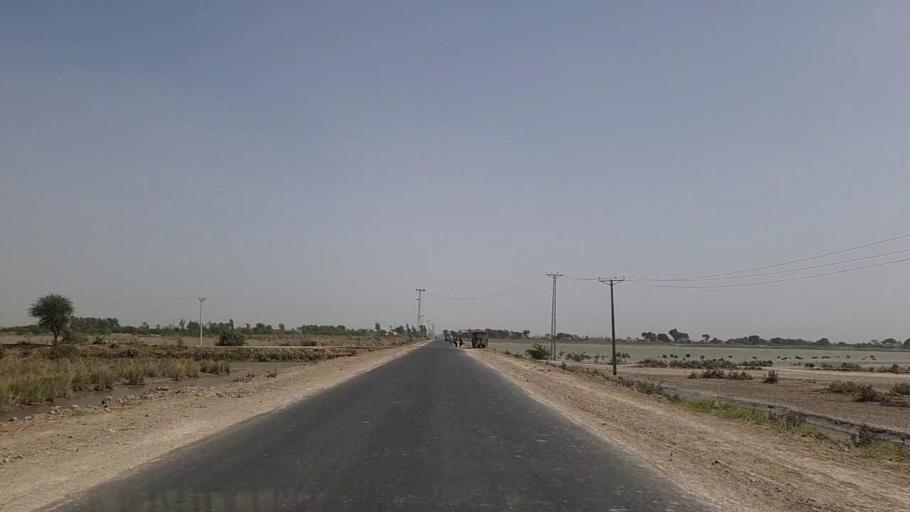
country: PK
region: Sindh
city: Tando Bago
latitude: 24.8069
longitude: 68.9330
